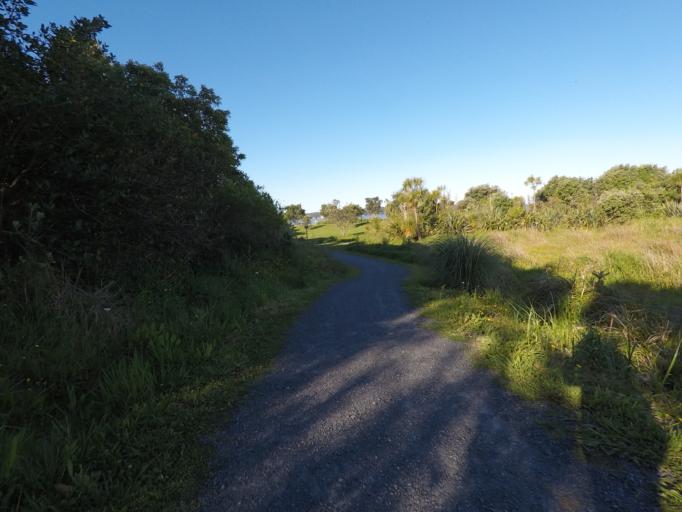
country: NZ
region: Auckland
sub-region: Auckland
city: Rosebank
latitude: -36.8402
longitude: 174.6605
